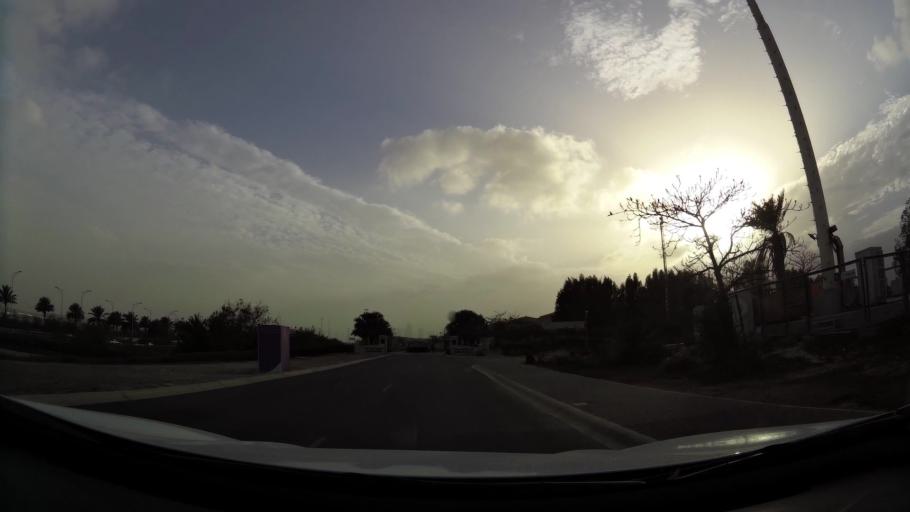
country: AE
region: Abu Dhabi
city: Abu Dhabi
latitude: 24.5396
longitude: 54.4365
